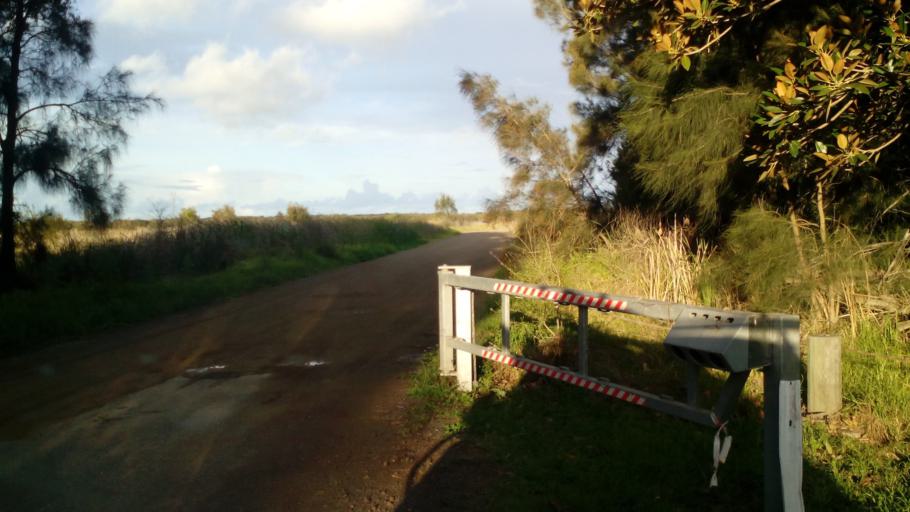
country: AU
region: New South Wales
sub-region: Newcastle
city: Mayfield West
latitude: -32.8414
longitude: 151.7152
